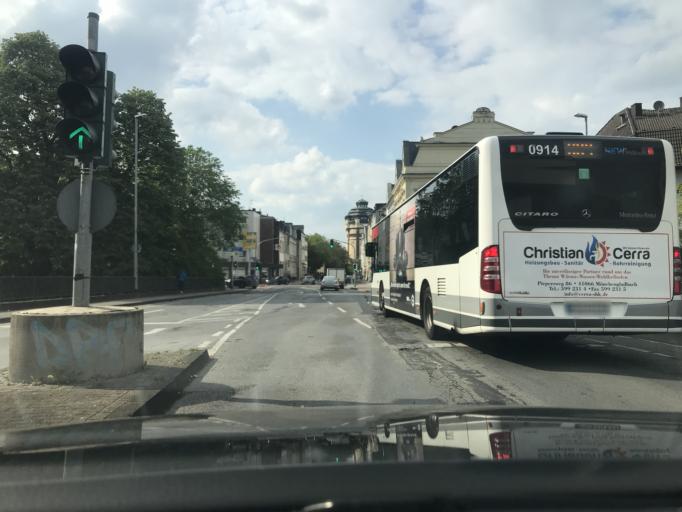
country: DE
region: North Rhine-Westphalia
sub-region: Regierungsbezirk Dusseldorf
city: Monchengladbach
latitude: 51.1984
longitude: 6.4294
